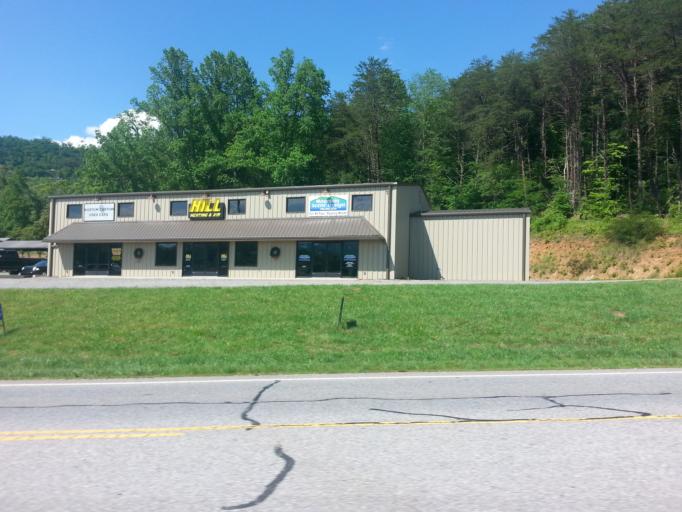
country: US
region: Georgia
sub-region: Towns County
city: Hiawassee
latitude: 34.9412
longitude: -83.7483
